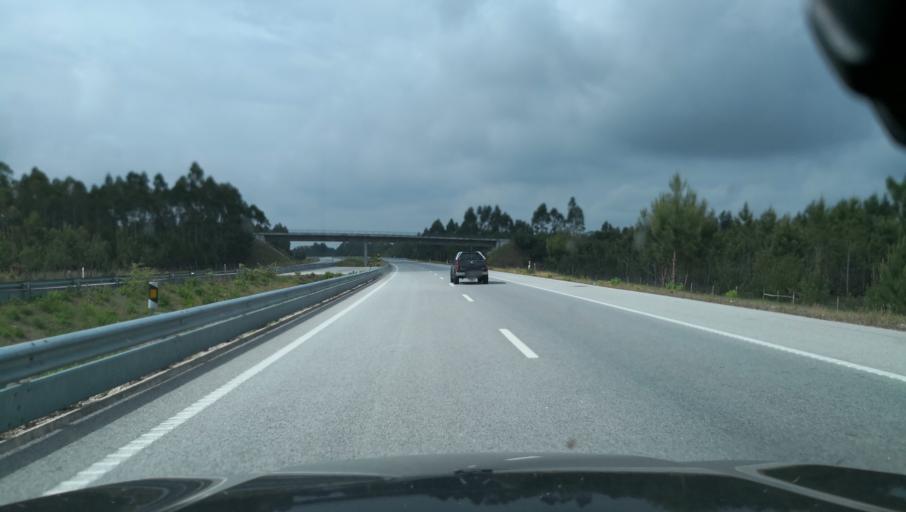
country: PT
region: Coimbra
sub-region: Figueira da Foz
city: Alhadas
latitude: 40.2775
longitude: -8.7564
